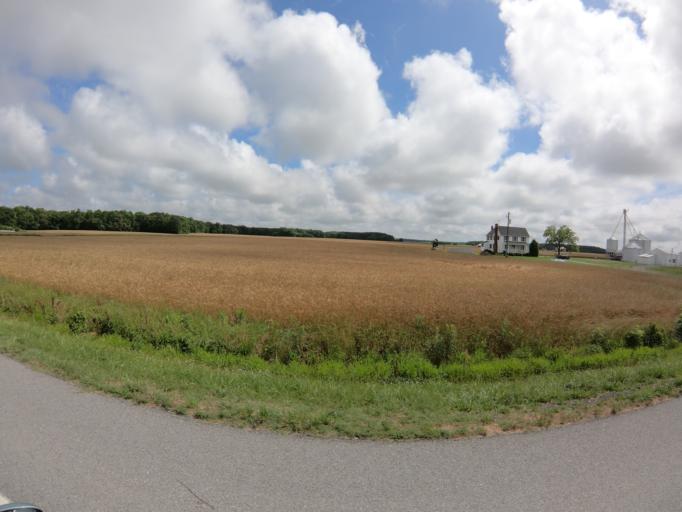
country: US
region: Maryland
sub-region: Caroline County
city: Greensboro
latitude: 39.0966
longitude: -75.8841
